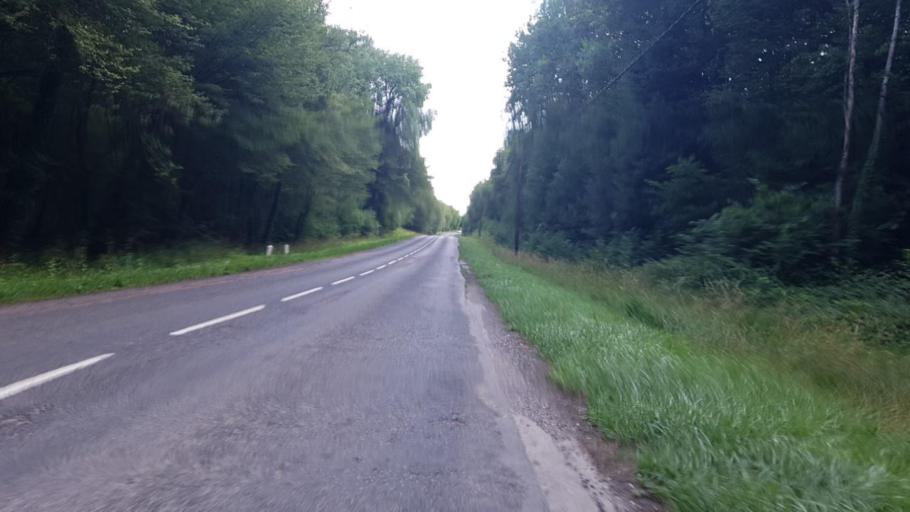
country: FR
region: Picardie
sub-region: Departement de l'Aisne
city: Crezancy
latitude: 49.0771
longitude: 3.5238
